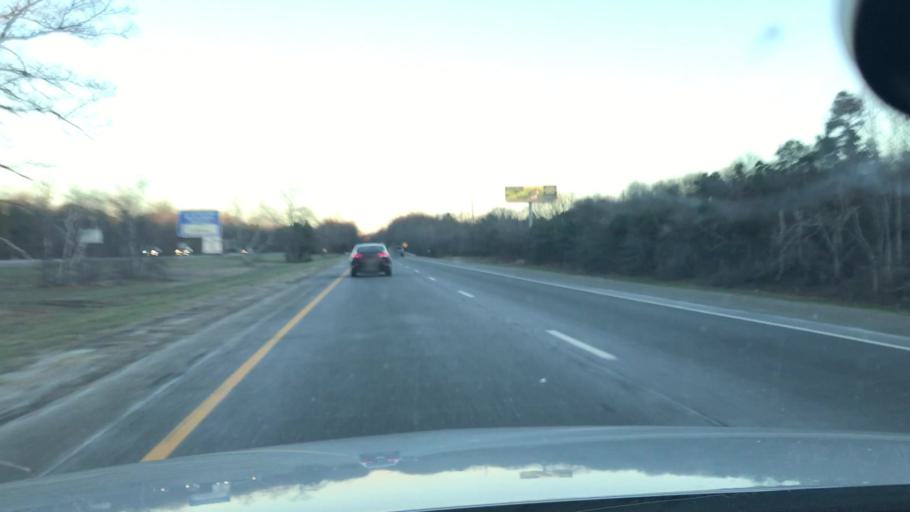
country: US
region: New Jersey
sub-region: Camden County
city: Sicklerville
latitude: 39.7277
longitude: -75.0033
